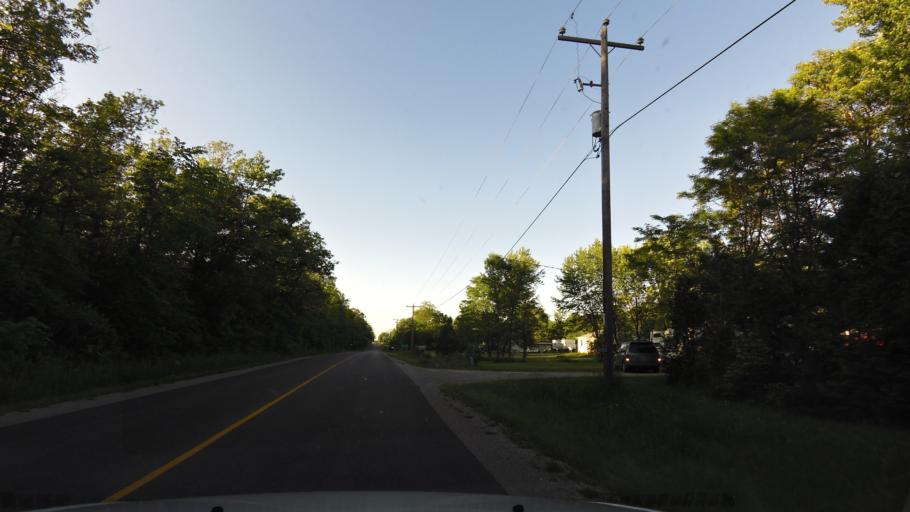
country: CA
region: Ontario
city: Ancaster
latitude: 43.0252
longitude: -80.0792
